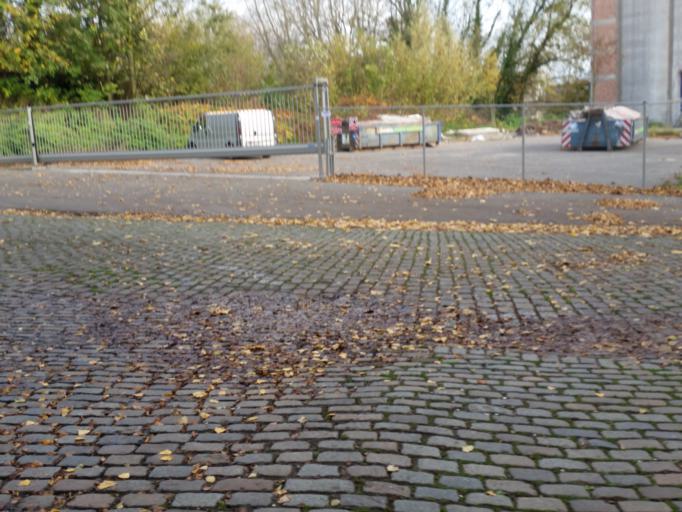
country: BE
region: Flanders
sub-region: Provincie Vlaams-Brabant
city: Diegem
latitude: 50.8954
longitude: 4.3963
